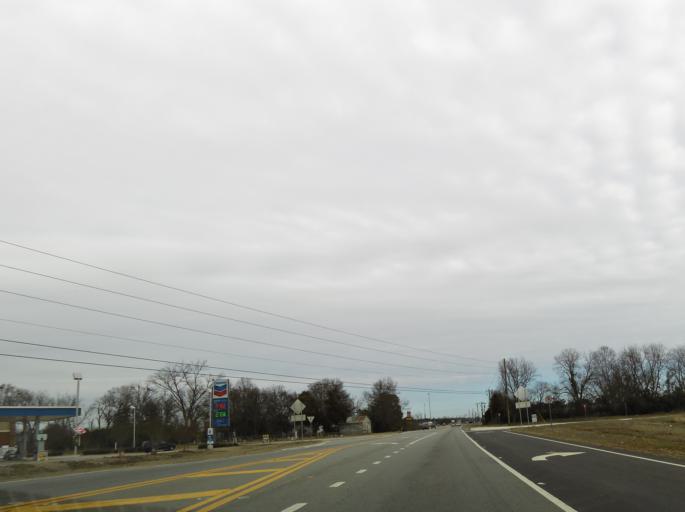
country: US
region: Georgia
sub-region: Peach County
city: Byron
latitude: 32.6099
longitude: -83.7470
